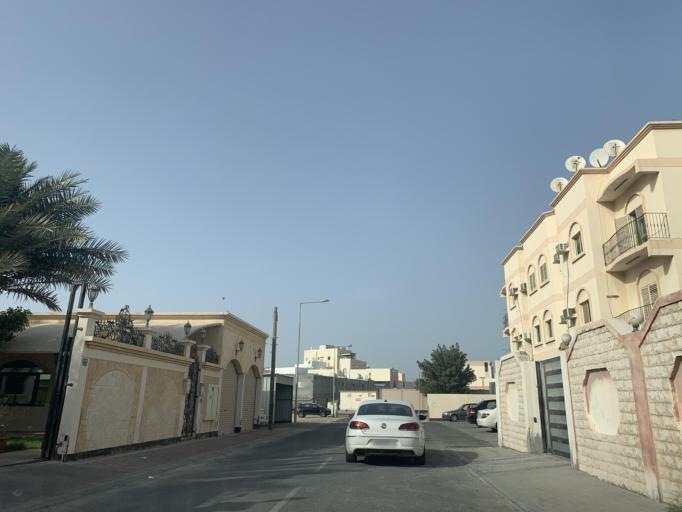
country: BH
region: Northern
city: Madinat `Isa
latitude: 26.1581
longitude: 50.5107
